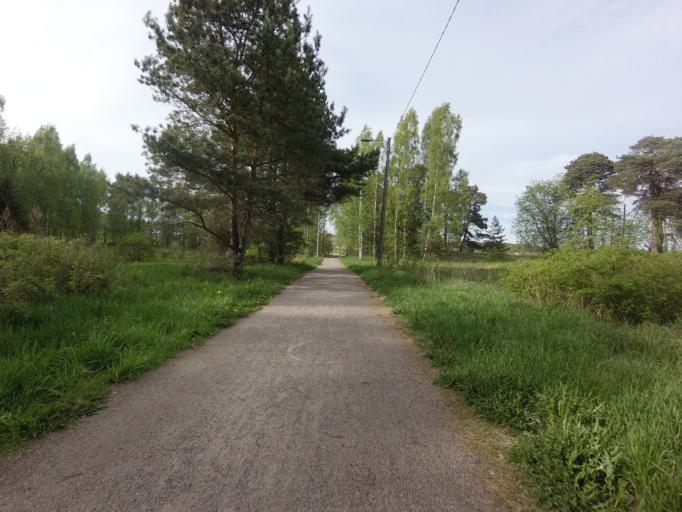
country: FI
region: Uusimaa
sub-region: Helsinki
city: Koukkuniemi
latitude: 60.1517
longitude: 24.6989
